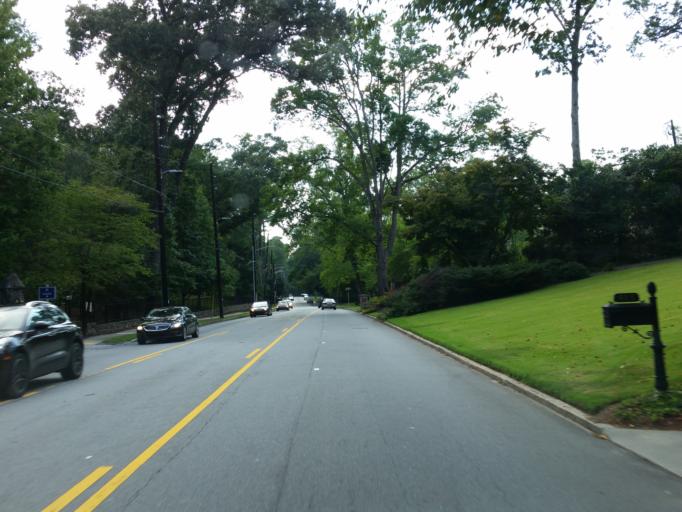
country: US
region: Georgia
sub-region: Cobb County
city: Vinings
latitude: 33.8503
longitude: -84.4169
